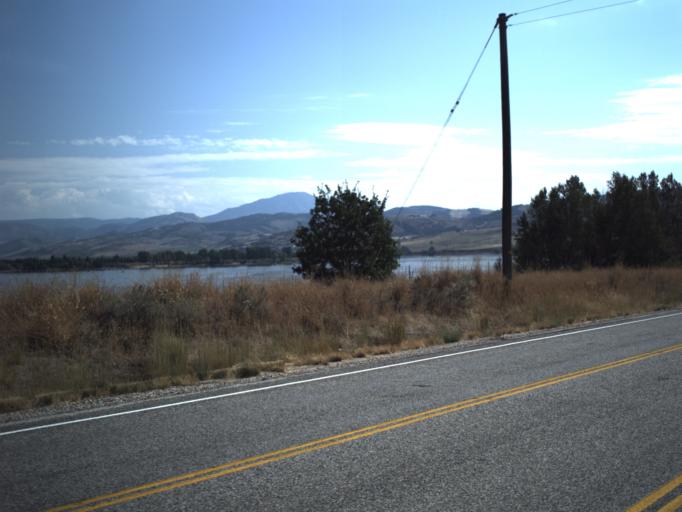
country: US
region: Utah
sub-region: Weber County
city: Wolf Creek
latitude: 41.2748
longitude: -111.8206
